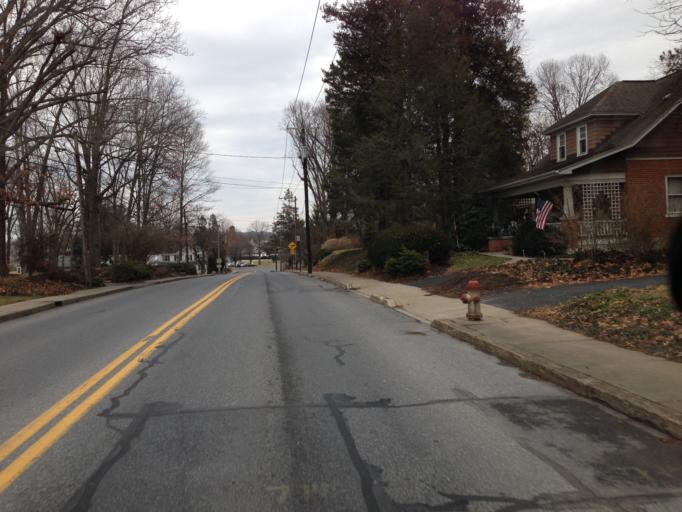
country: US
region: Pennsylvania
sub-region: Lancaster County
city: Lititz
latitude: 40.1483
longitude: -76.3106
